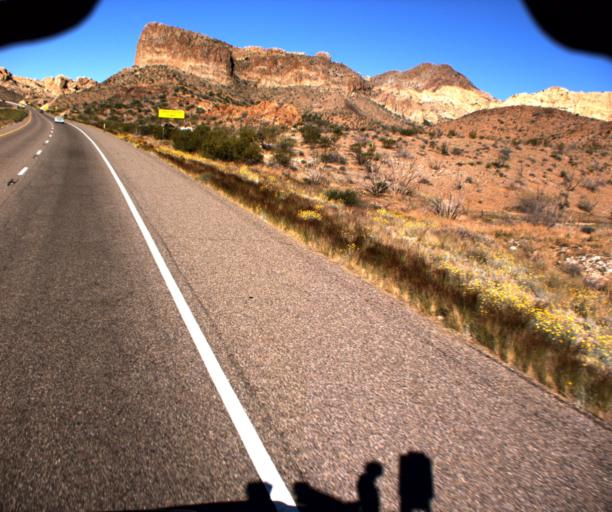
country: US
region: Arizona
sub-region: Mohave County
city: Golden Valley
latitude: 35.2279
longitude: -114.3759
